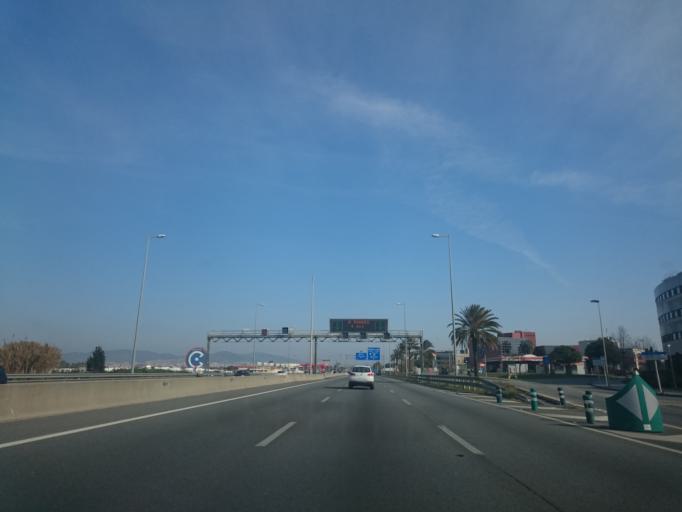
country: ES
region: Catalonia
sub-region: Provincia de Barcelona
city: El Prat de Llobregat
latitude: 41.3129
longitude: 2.0678
